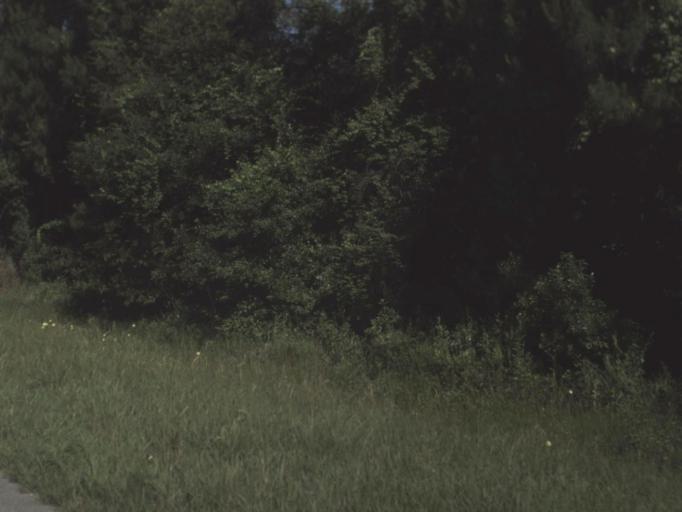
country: US
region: Florida
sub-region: Duval County
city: Baldwin
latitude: 30.3057
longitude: -81.9298
